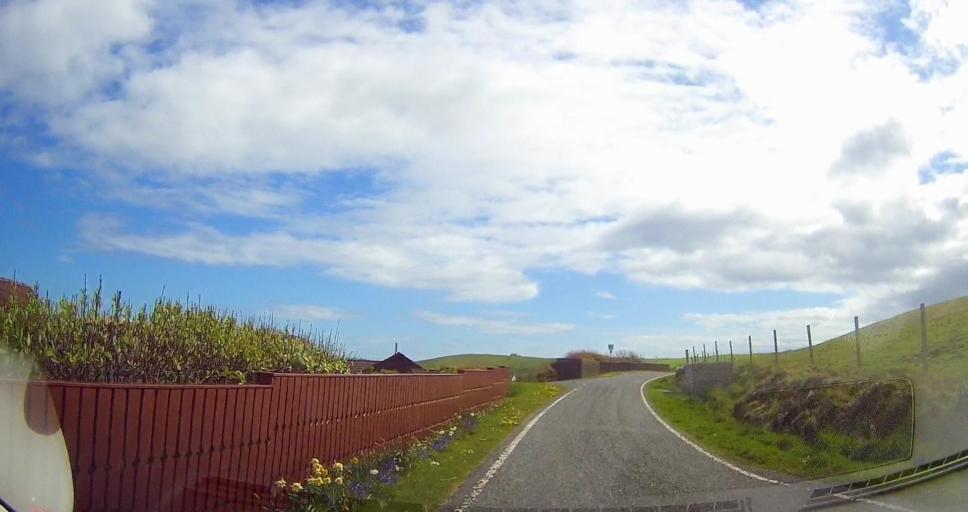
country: GB
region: Scotland
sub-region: Shetland Islands
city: Sandwick
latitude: 59.9313
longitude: -1.3450
